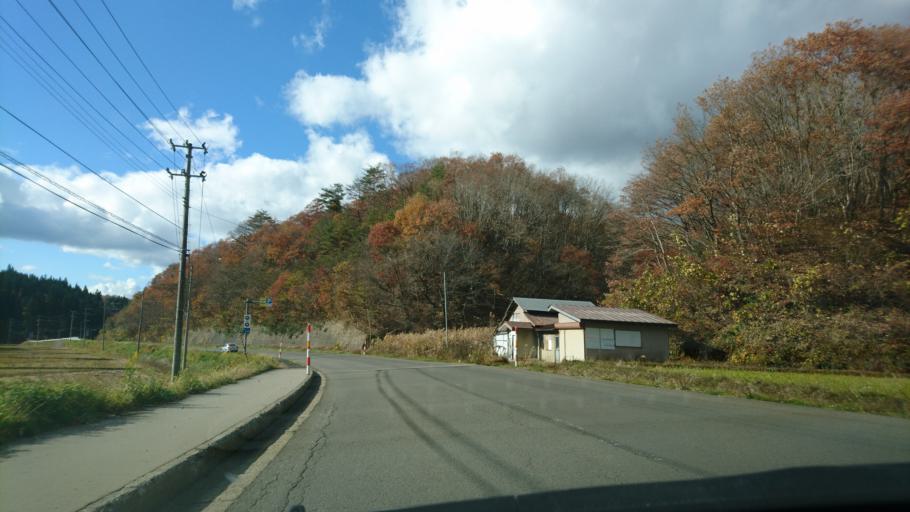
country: JP
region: Akita
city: Yuzawa
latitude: 39.2820
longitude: 140.3311
